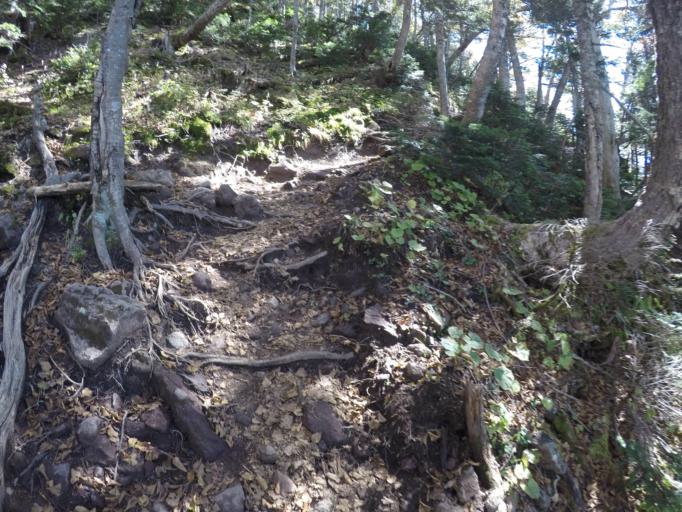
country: JP
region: Tochigi
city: Nikko
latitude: 36.7973
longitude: 139.3697
